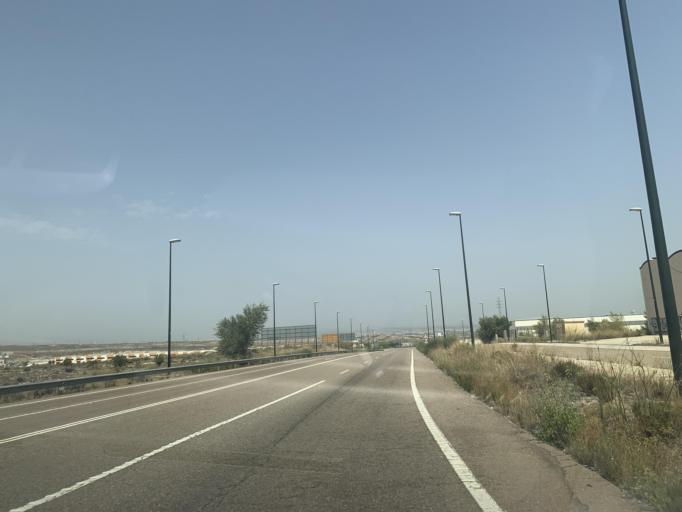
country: ES
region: Aragon
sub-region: Provincia de Zaragoza
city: El Burgo de Ebro
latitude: 41.5824
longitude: -0.8268
